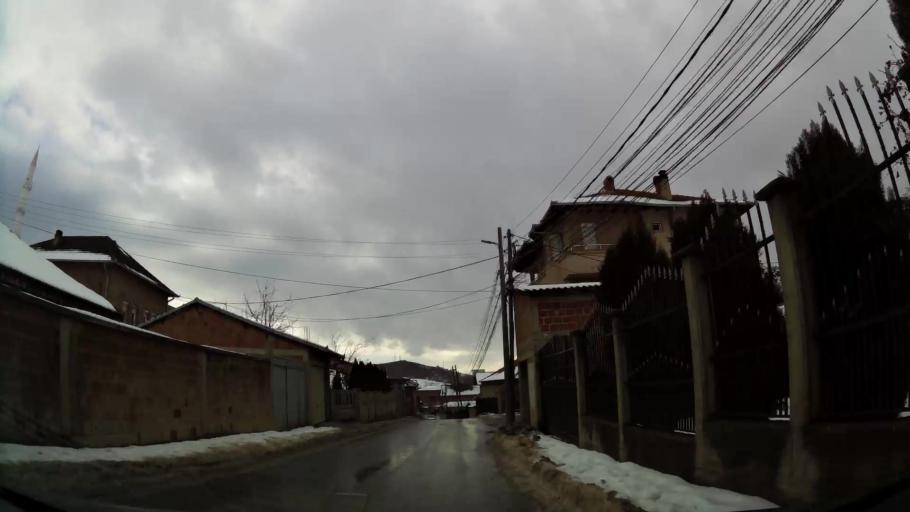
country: XK
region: Pristina
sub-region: Komuna e Prishtines
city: Pristina
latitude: 42.6727
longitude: 21.1851
